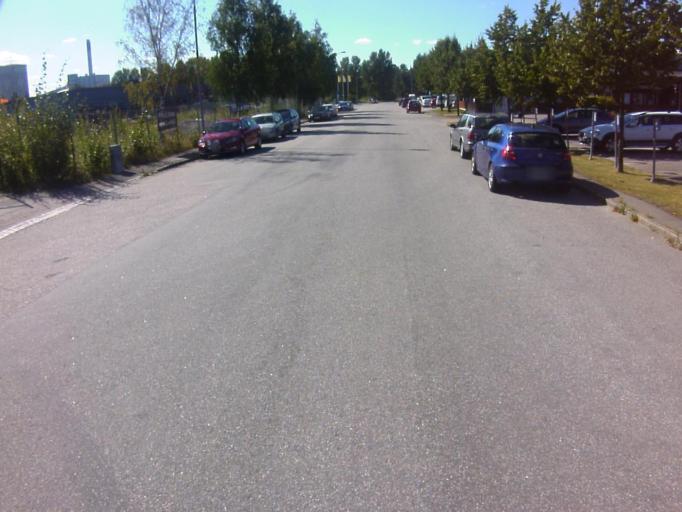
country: SE
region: Soedermanland
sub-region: Eskilstuna Kommun
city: Eskilstuna
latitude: 59.3863
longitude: 16.4926
